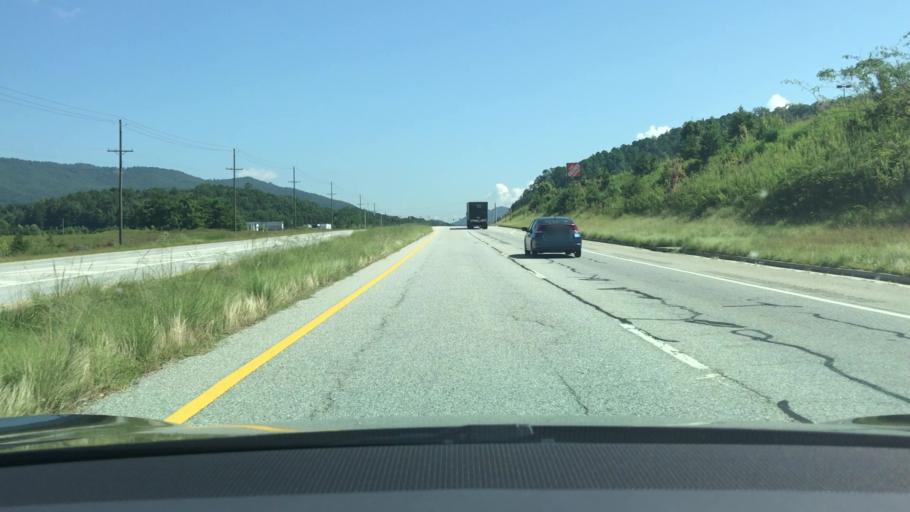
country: US
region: Georgia
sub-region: Rabun County
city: Clayton
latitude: 34.8555
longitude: -83.4078
